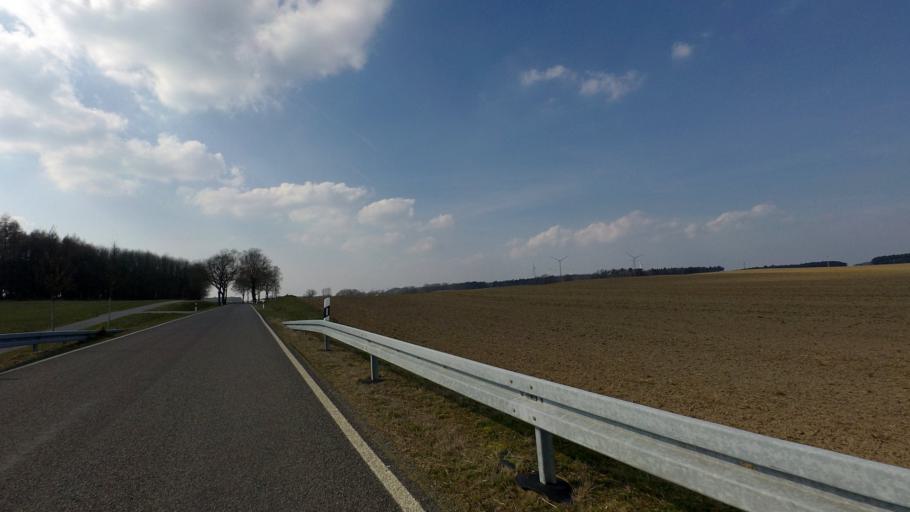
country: DE
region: Brandenburg
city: Ihlow
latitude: 51.9483
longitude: 13.3810
